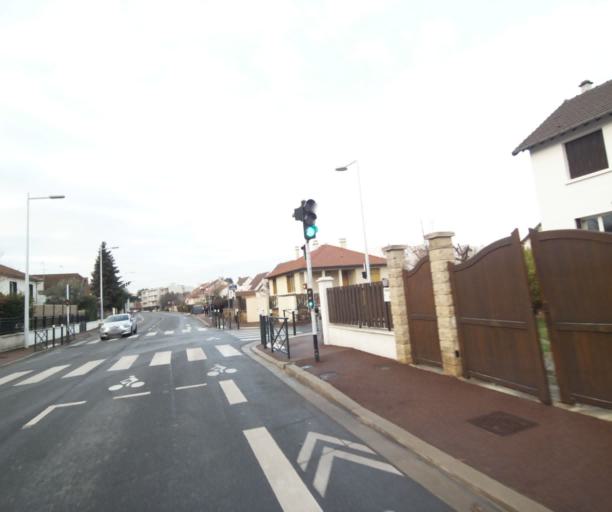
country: FR
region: Ile-de-France
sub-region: Departement des Hauts-de-Seine
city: Nanterre
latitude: 48.8781
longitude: 2.2051
